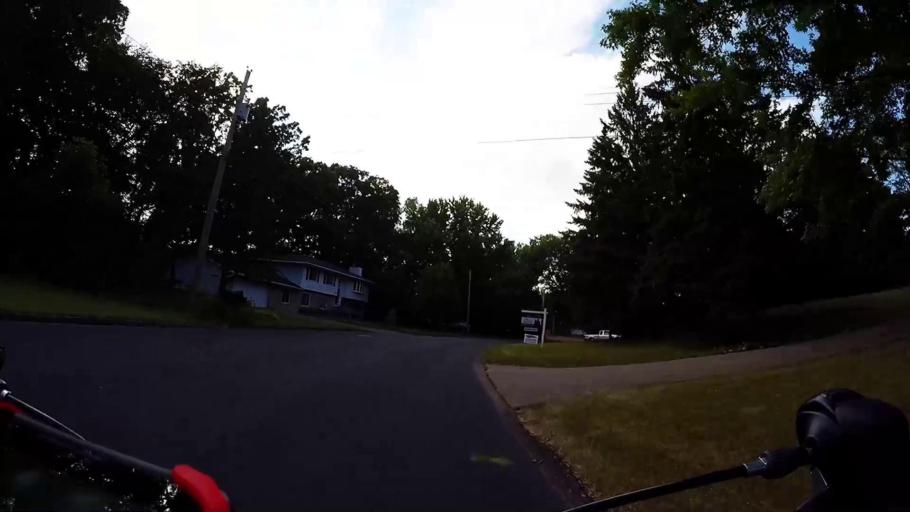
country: US
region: Minnesota
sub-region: Hennepin County
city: Eden Prairie
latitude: 44.8829
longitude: -93.4787
